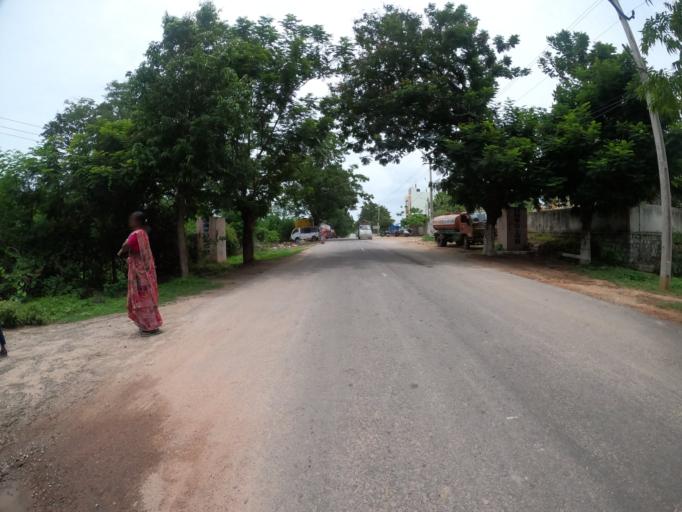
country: IN
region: Telangana
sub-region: Hyderabad
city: Hyderabad
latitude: 17.3414
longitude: 78.3609
